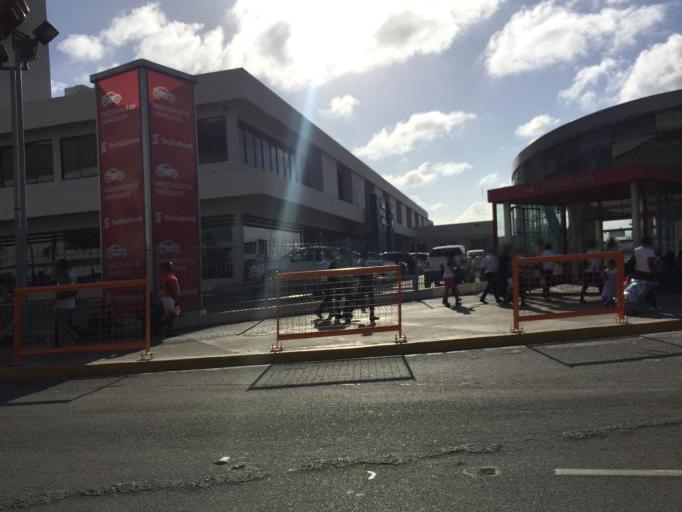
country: DO
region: Nacional
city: La Agustina
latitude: 18.4839
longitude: -69.9406
